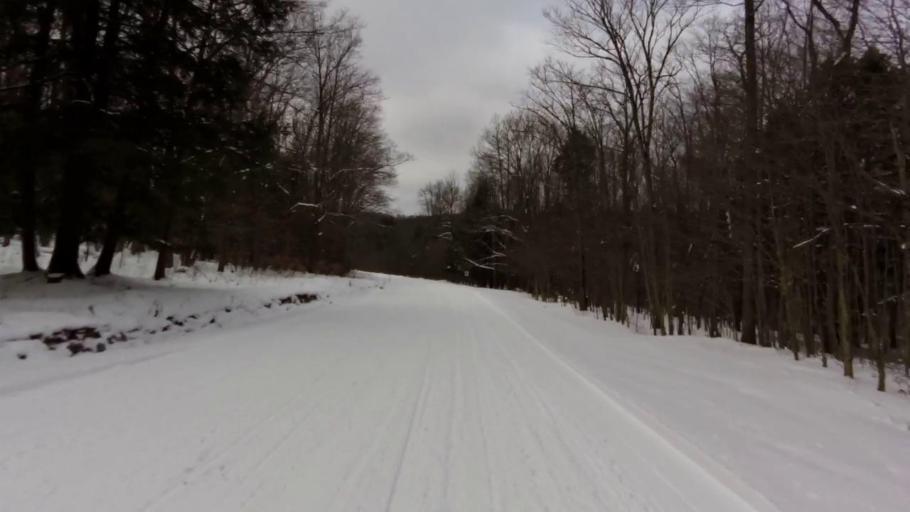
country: US
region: New York
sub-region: Cattaraugus County
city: Salamanca
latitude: 42.0343
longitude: -78.8011
